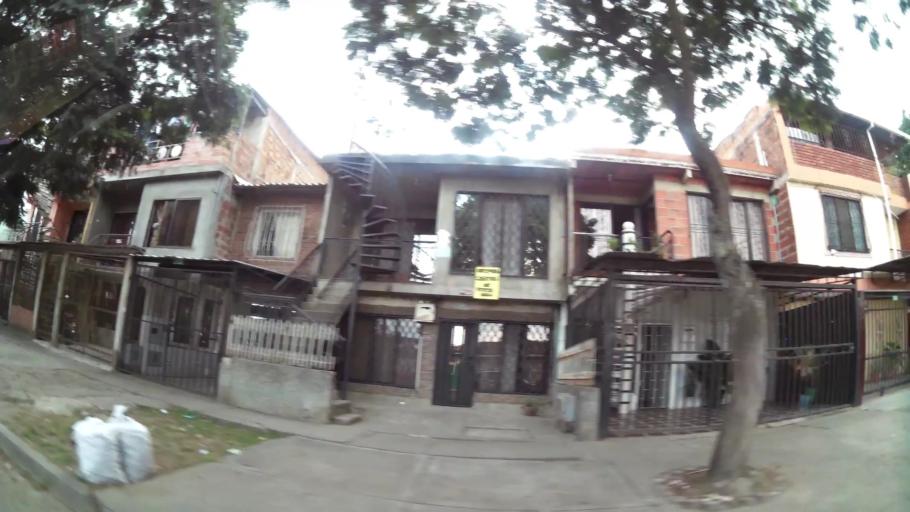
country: CO
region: Valle del Cauca
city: Cali
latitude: 3.4629
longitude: -76.4874
